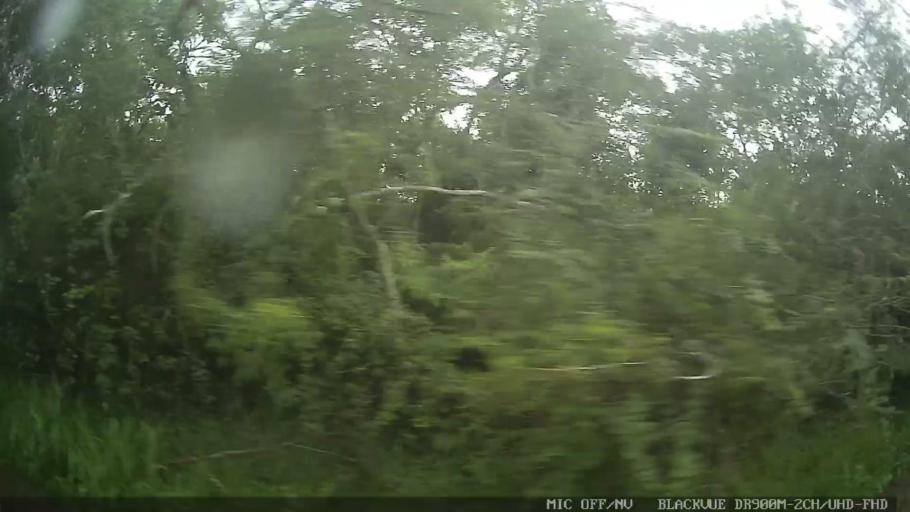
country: BR
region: Sao Paulo
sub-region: Ribeirao Pires
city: Ribeirao Pires
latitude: -23.6940
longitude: -46.4008
